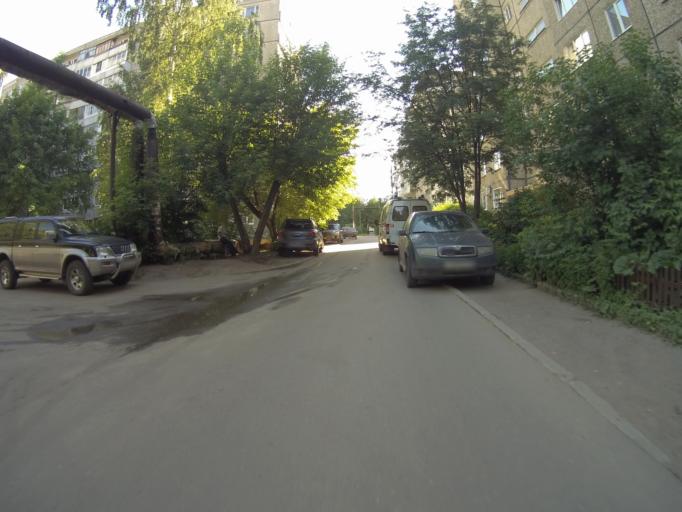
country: RU
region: Vladimir
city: Kommunar
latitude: 56.1619
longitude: 40.4656
